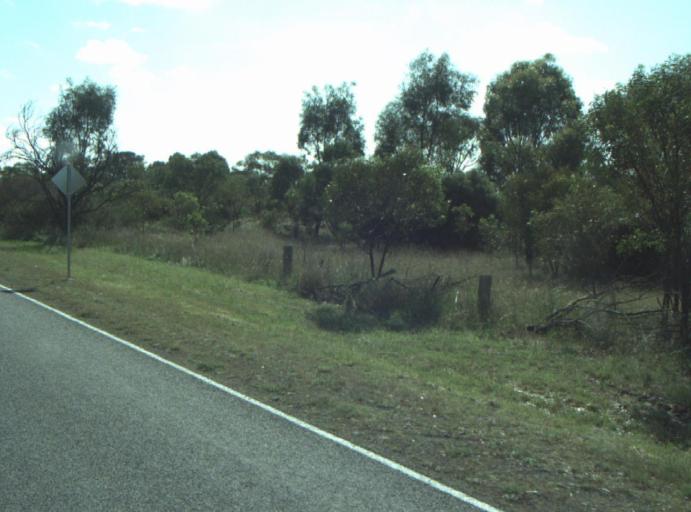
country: AU
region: Victoria
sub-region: Greater Geelong
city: Lara
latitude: -38.0049
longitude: 144.4358
